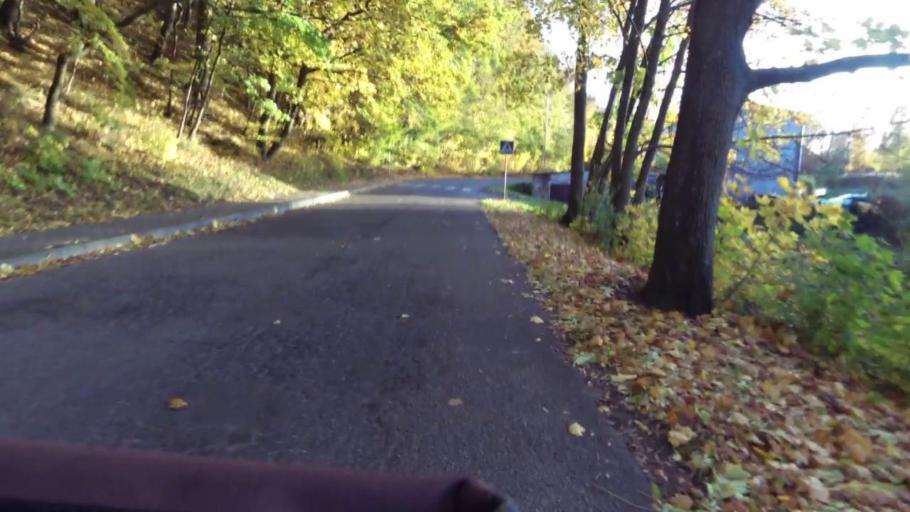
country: PL
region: West Pomeranian Voivodeship
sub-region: Powiat kamienski
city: Miedzyzdroje
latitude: 53.8788
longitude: 14.4292
